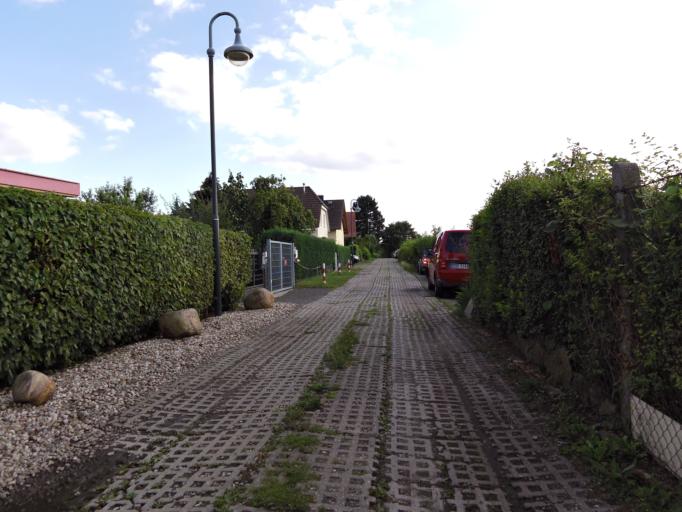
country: DE
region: Saxony
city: Taucha
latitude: 51.3367
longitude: 12.4400
